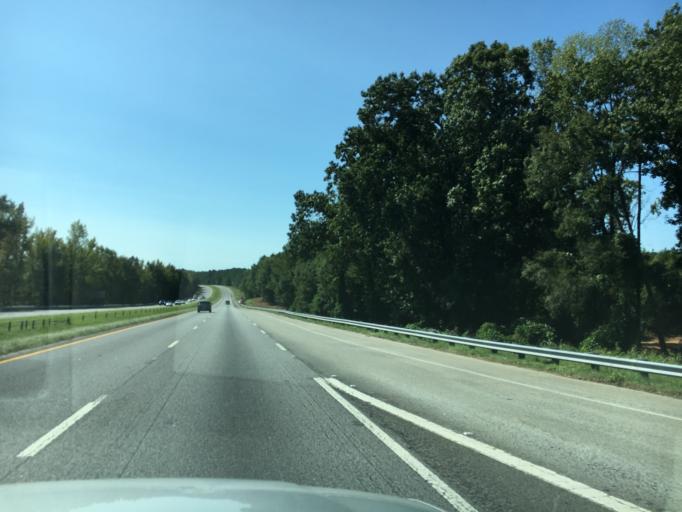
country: US
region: South Carolina
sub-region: Spartanburg County
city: Woodruff
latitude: 34.7454
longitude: -81.9547
